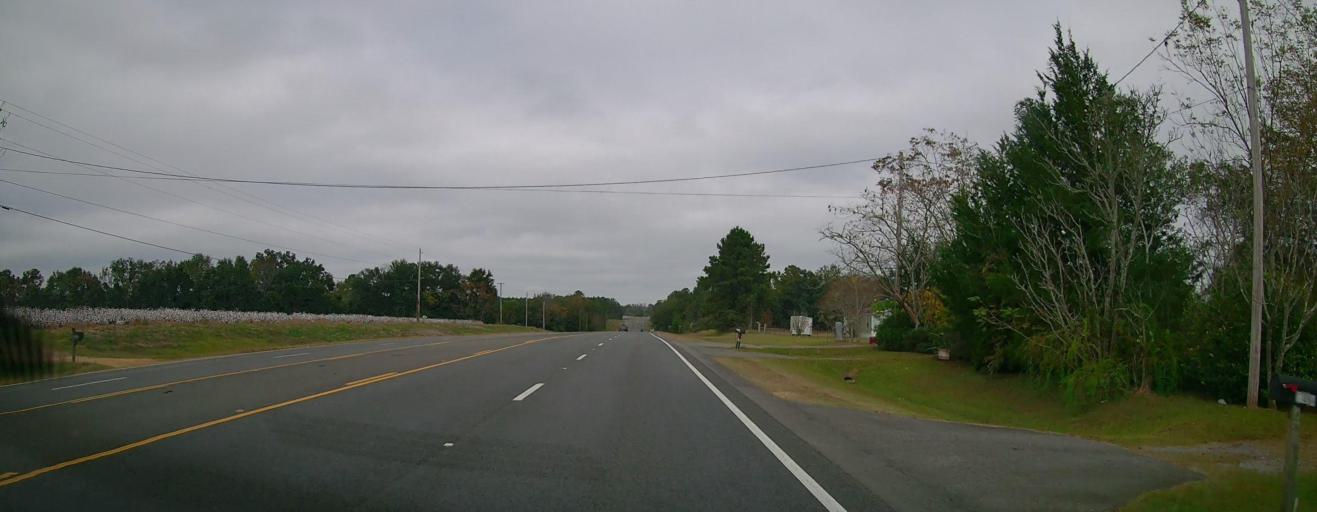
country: US
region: Georgia
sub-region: Thomas County
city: Thomasville
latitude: 30.9295
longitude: -83.9121
